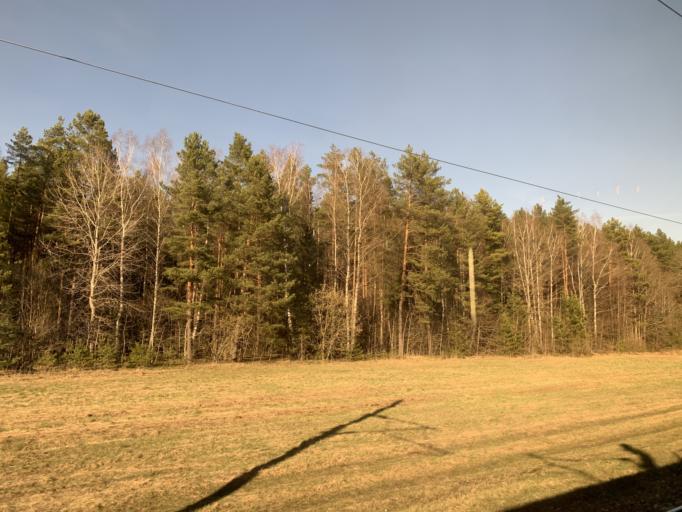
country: BY
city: Soly
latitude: 54.4914
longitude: 26.2923
